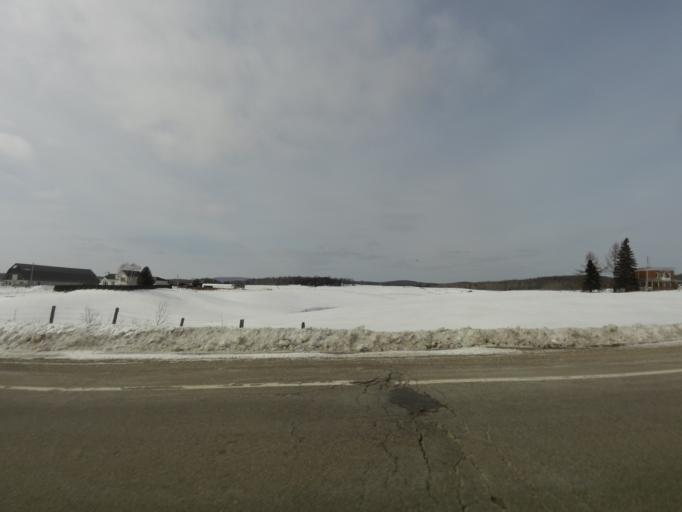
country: CA
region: Quebec
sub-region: Laurentides
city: Ferme-Neuve
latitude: 46.7242
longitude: -75.3969
